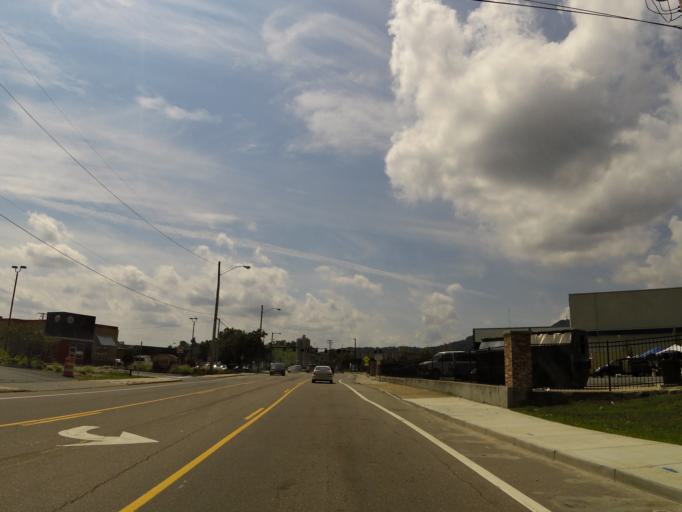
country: US
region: Tennessee
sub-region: Sullivan County
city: Kingsport
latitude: 36.5515
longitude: -82.5642
